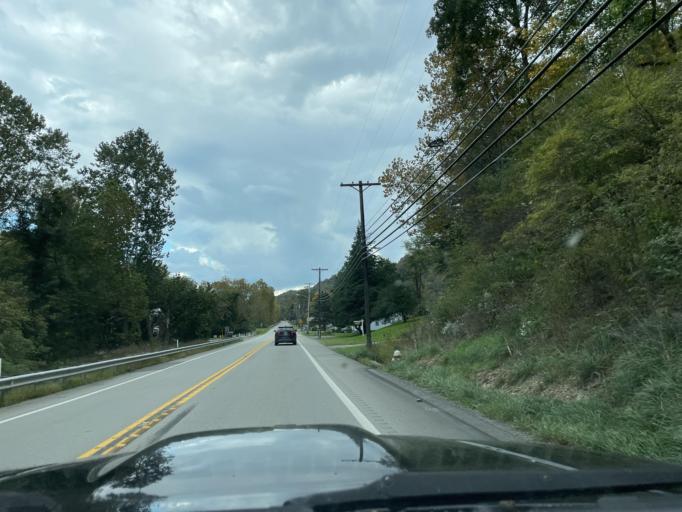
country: US
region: Pennsylvania
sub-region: Westmoreland County
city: Lower Burrell
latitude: 40.5391
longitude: -79.7210
